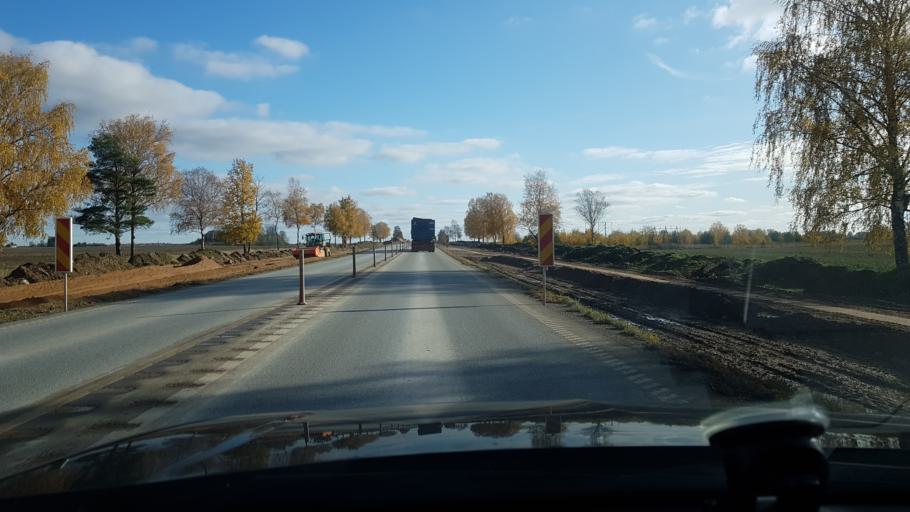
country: EE
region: Laeaene-Virumaa
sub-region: Haljala vald
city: Haljala
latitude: 59.4297
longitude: 26.2186
